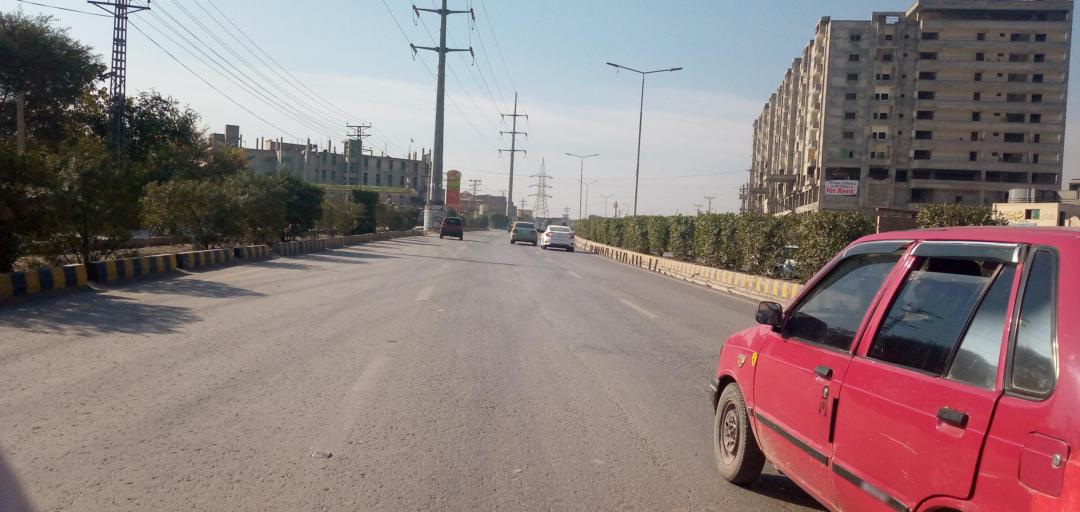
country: PK
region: Khyber Pakhtunkhwa
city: Peshawar
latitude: 33.9642
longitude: 71.5302
